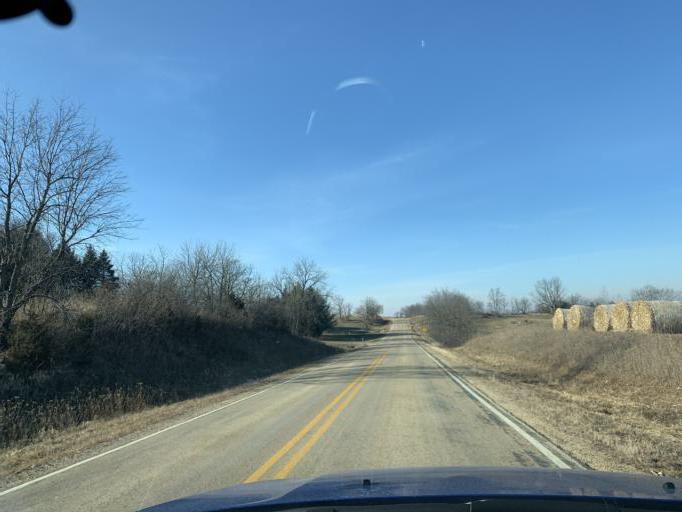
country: US
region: Wisconsin
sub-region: Iowa County
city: Barneveld
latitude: 42.8115
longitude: -89.8946
